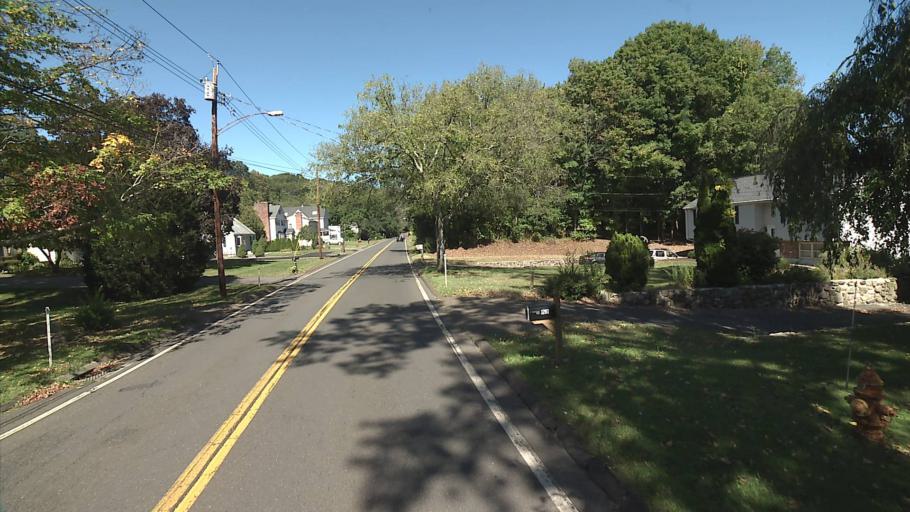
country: US
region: Connecticut
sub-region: New Haven County
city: Woodbridge
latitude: 41.3493
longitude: -72.9831
